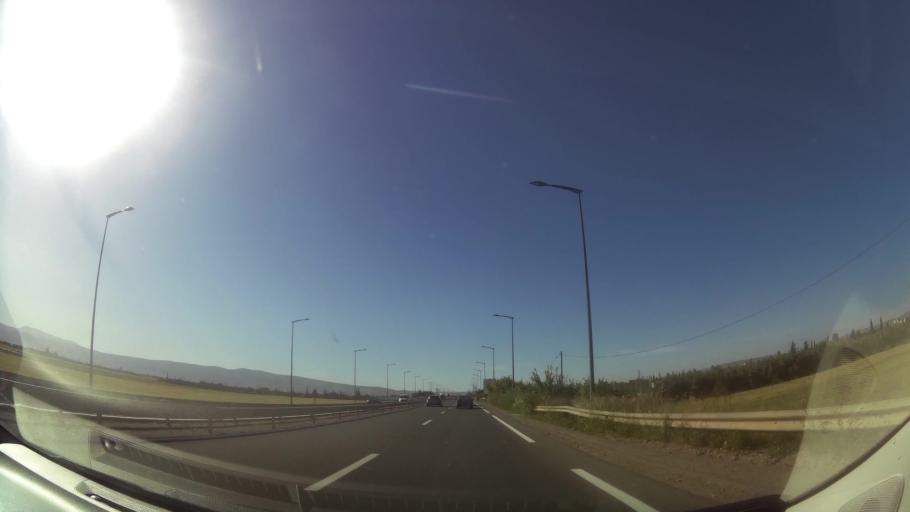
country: MA
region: Oriental
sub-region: Oujda-Angad
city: Oujda
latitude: 34.8213
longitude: -1.9682
